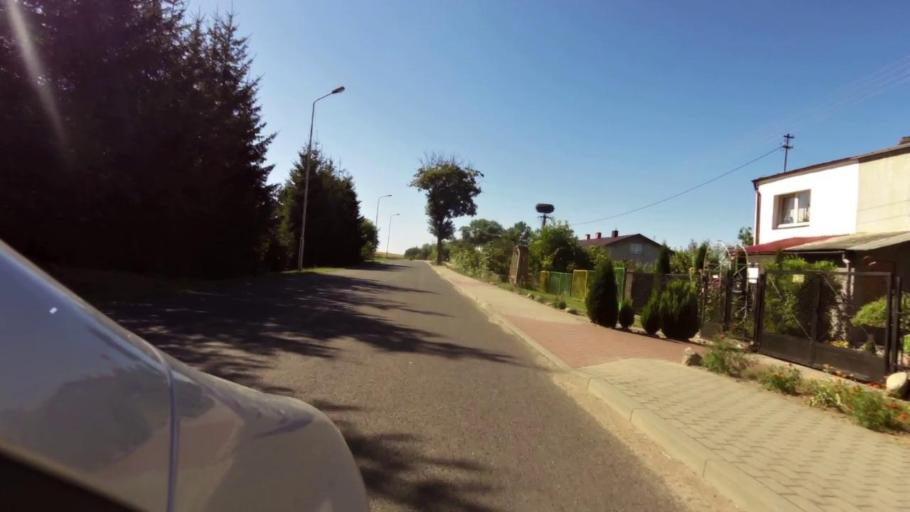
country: PL
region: West Pomeranian Voivodeship
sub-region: Powiat szczecinecki
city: Bialy Bor
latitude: 53.8177
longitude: 16.8134
